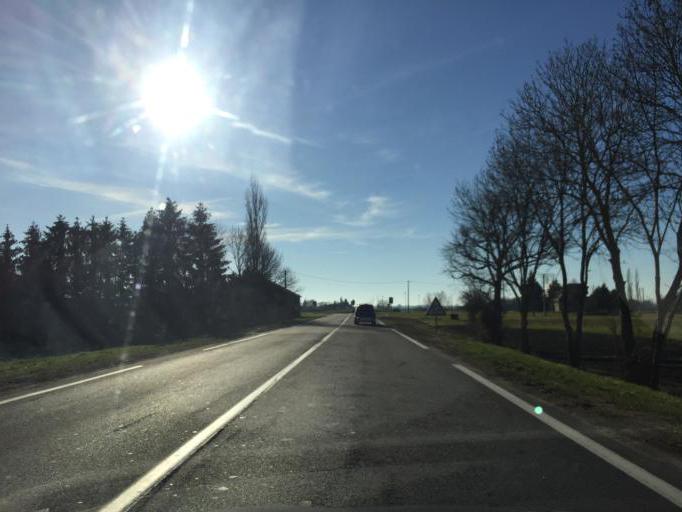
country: FR
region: Auvergne
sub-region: Departement de l'Allier
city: Saint-Pourcain-sur-Sioule
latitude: 46.2668
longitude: 3.2894
